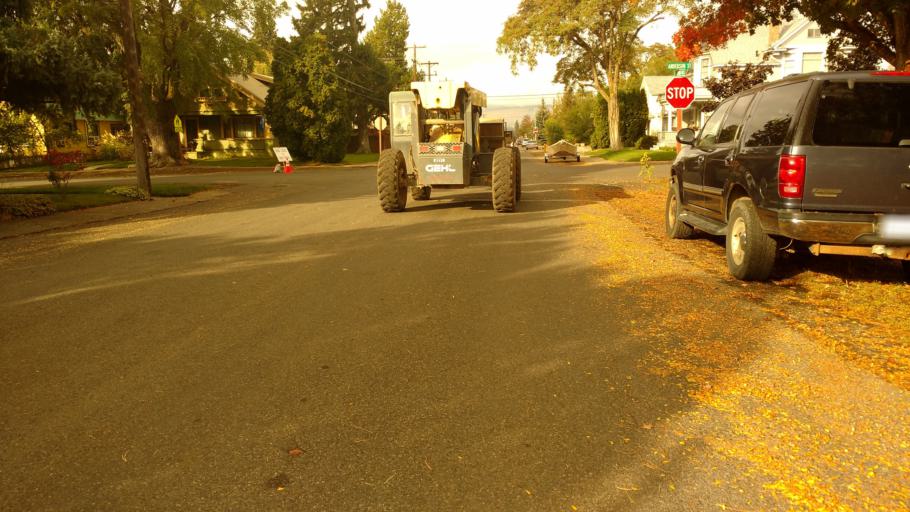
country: US
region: Washington
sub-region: Kittitas County
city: Ellensburg
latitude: 46.9936
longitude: -120.5414
